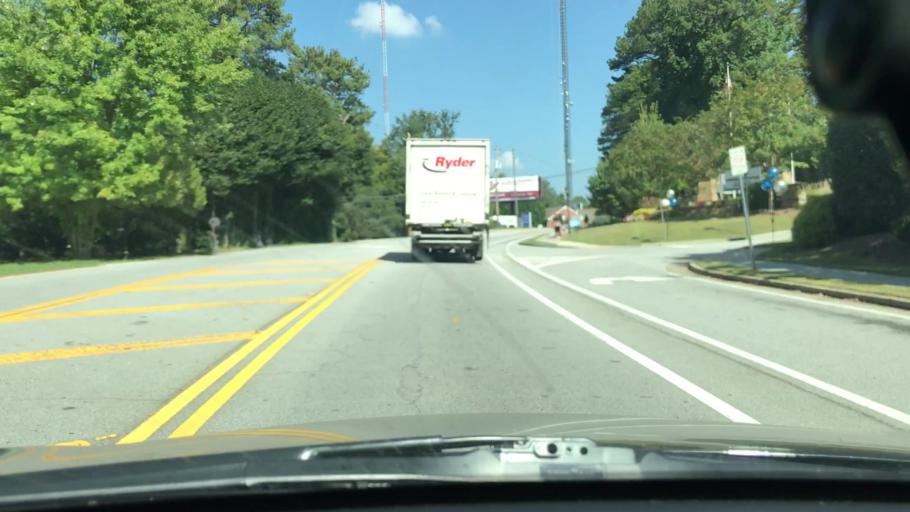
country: US
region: Georgia
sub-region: DeKalb County
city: Druid Hills
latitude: 33.8022
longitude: -84.3378
